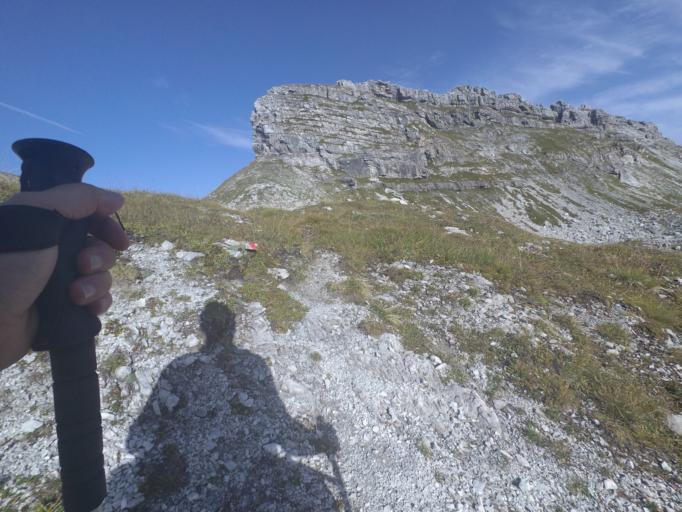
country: AT
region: Salzburg
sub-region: Politischer Bezirk Sankt Johann im Pongau
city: Kleinarl
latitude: 47.2224
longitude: 13.4127
